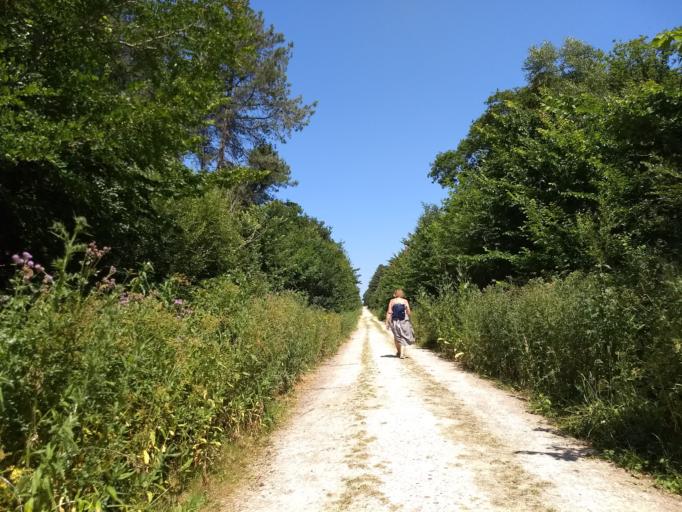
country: GB
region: England
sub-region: Isle of Wight
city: Newport
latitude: 50.7052
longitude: -1.3314
